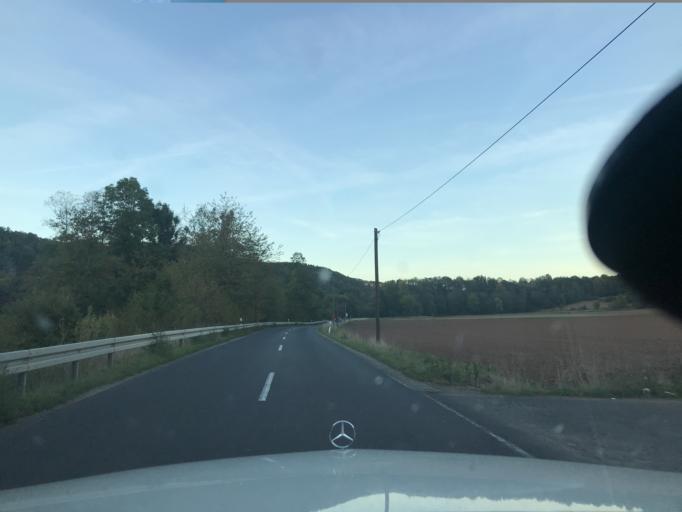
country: DE
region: Thuringia
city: Sickerode
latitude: 51.2047
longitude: 10.1263
